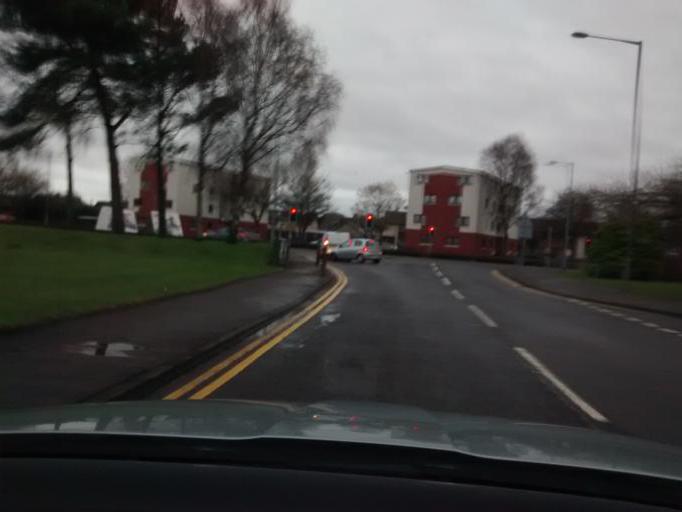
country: GB
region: Scotland
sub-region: Falkirk
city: Falkirk
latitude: 56.0051
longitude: -3.7650
